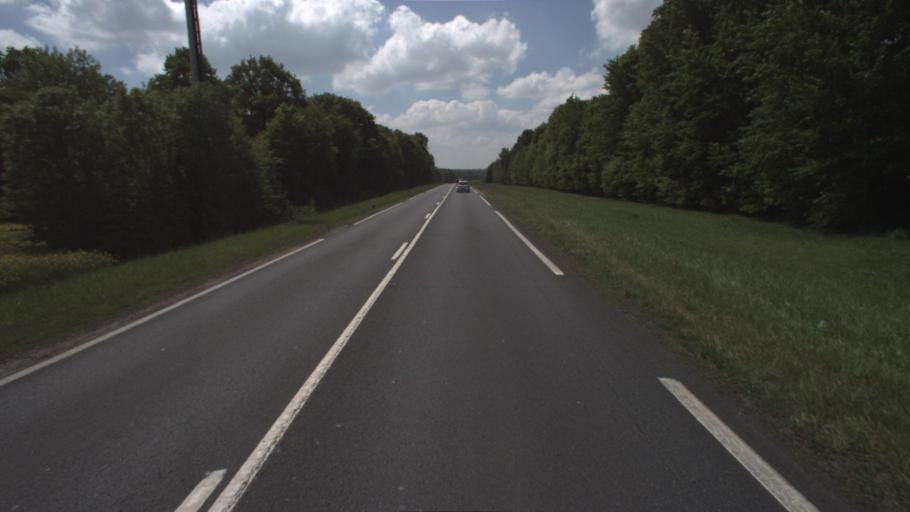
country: FR
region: Ile-de-France
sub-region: Departement de Seine-et-Marne
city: Chaumes-en-Brie
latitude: 48.6695
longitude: 2.8118
